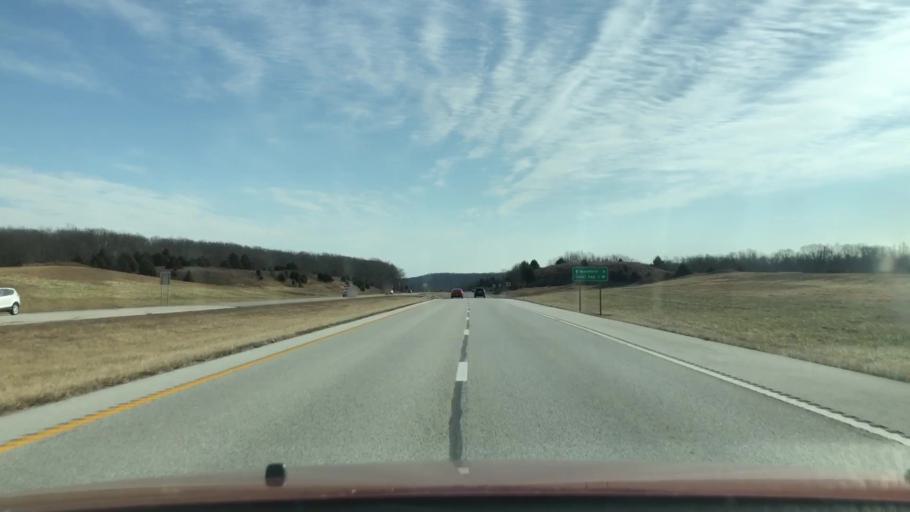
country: US
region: Missouri
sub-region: Webster County
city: Seymour
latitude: 37.1160
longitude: -92.6771
